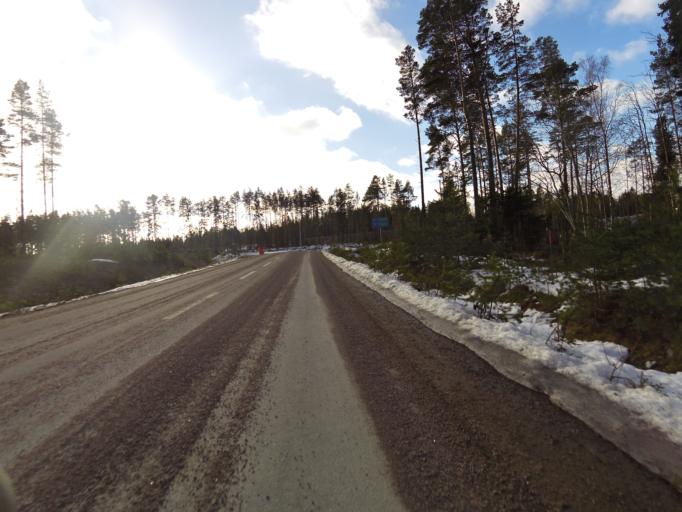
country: SE
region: Uppsala
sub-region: Alvkarleby Kommun
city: Skutskaer
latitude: 60.6508
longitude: 17.3460
